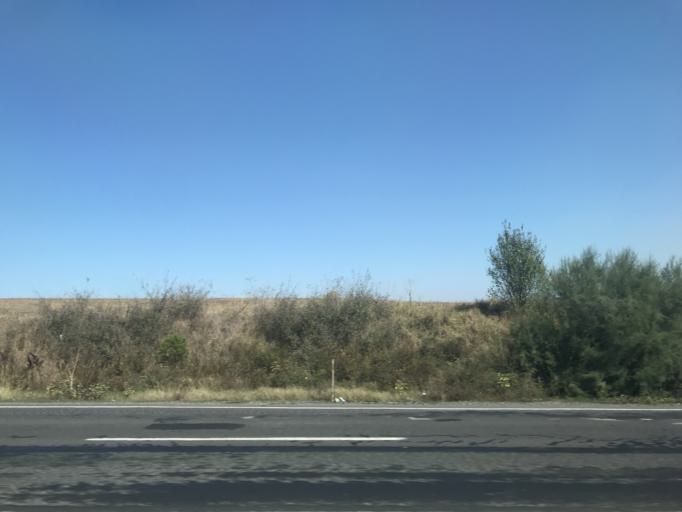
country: TR
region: Tekirdag
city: Muratli
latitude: 41.0908
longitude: 27.4930
